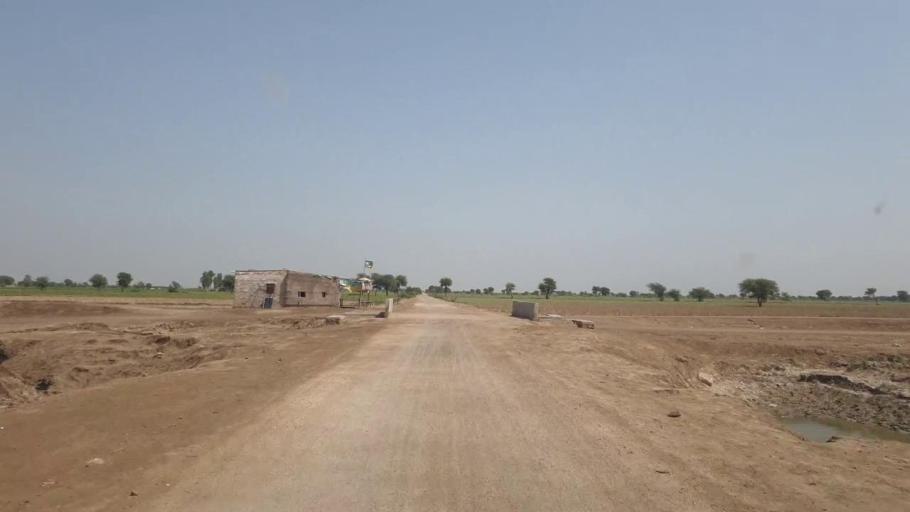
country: PK
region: Sindh
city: Jati
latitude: 24.4774
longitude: 68.5637
